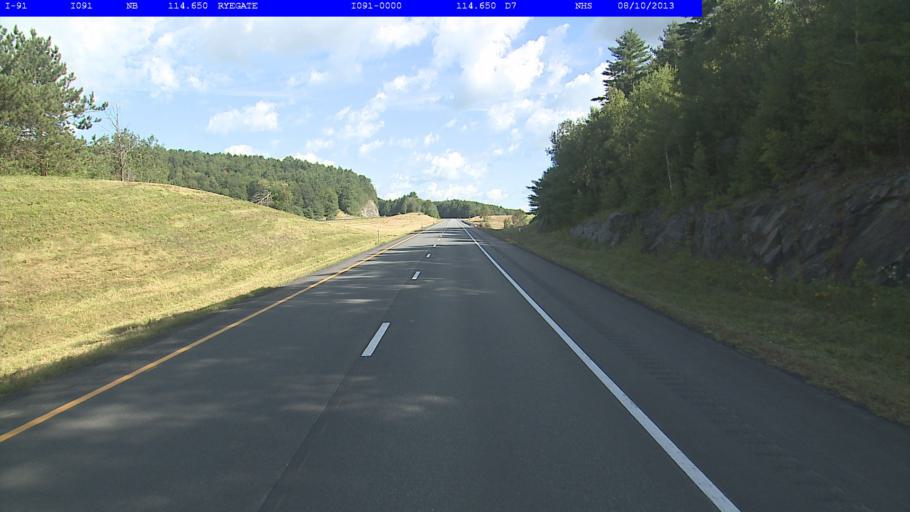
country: US
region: New Hampshire
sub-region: Grafton County
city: Woodsville
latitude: 44.2197
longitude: -72.0669
